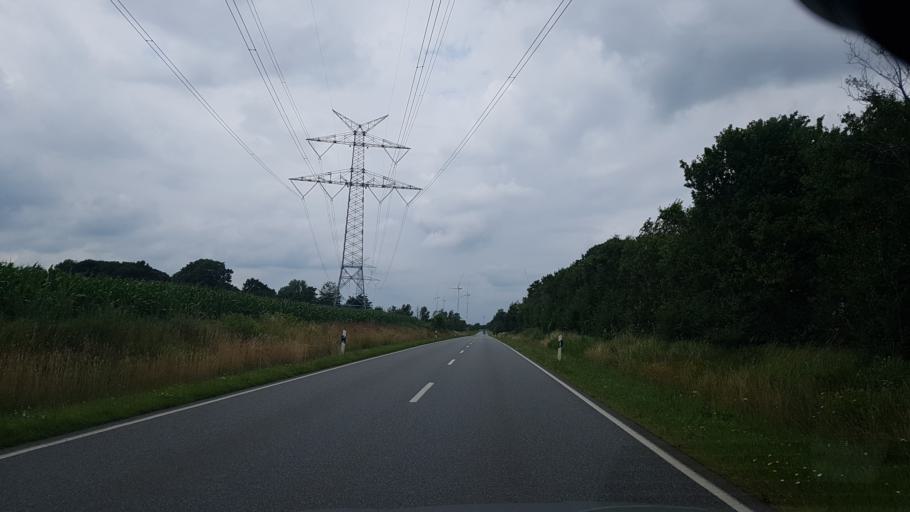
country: DE
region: Schleswig-Holstein
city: Jardelund
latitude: 54.8315
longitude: 9.2160
